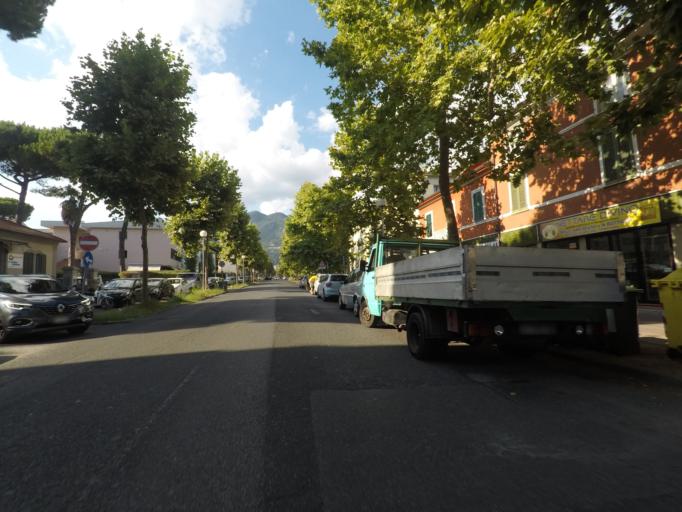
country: IT
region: Tuscany
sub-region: Provincia di Massa-Carrara
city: Massa
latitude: 44.0279
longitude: 10.1369
